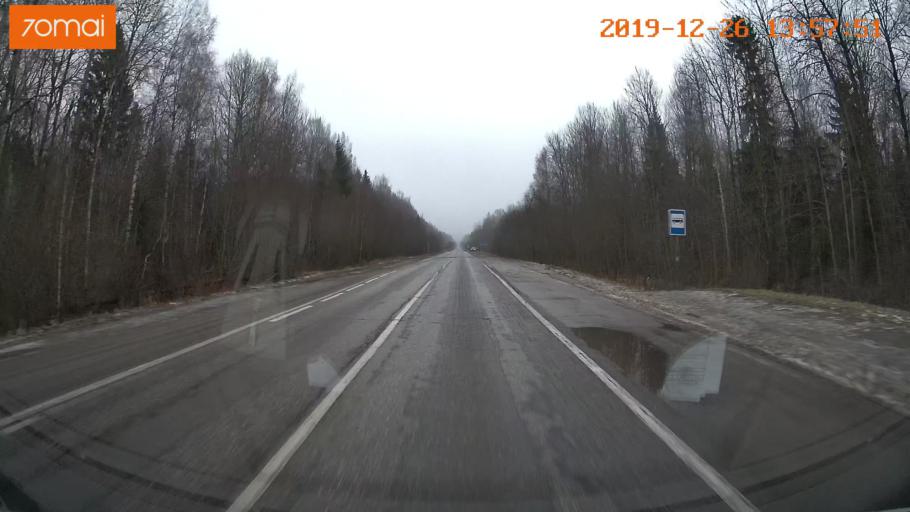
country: RU
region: Jaroslavl
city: Poshekhon'ye
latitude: 58.5789
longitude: 38.6881
